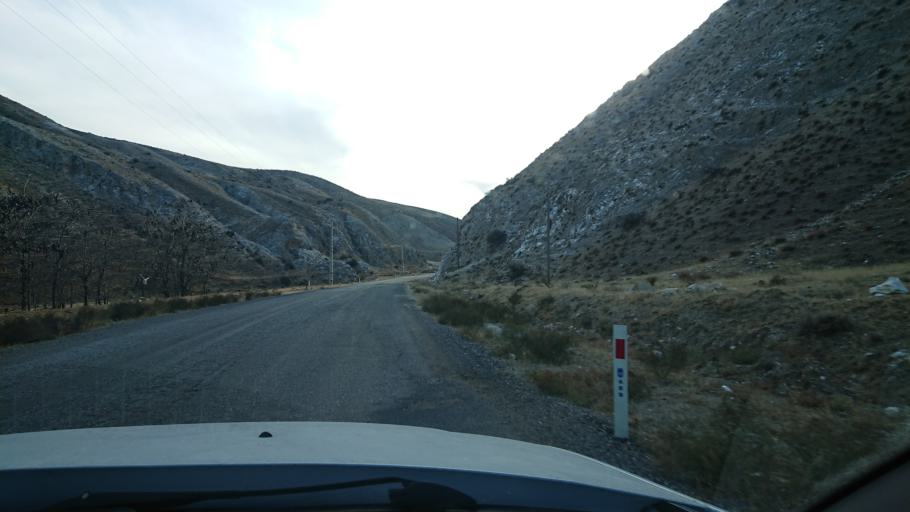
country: TR
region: Ankara
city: Sereflikochisar
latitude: 38.7533
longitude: 33.6923
